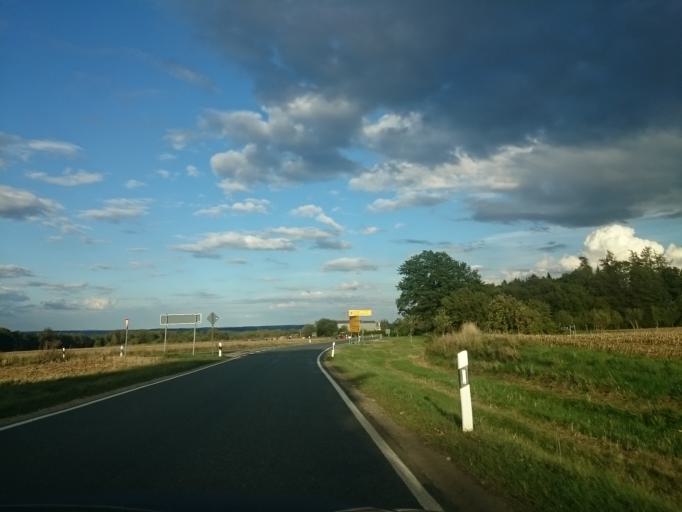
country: DE
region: Bavaria
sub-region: Regierungsbezirk Mittelfranken
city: Thalmassing
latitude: 49.0727
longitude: 11.1996
